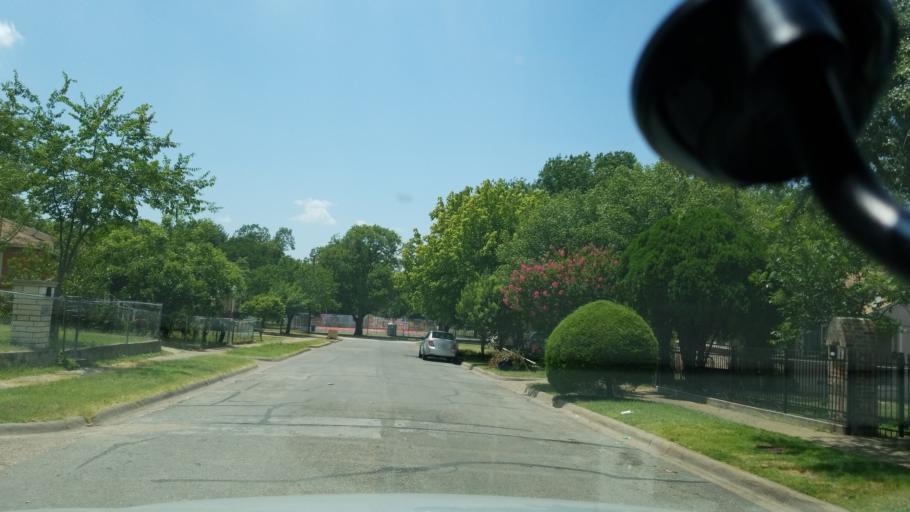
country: US
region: Texas
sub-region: Dallas County
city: Cockrell Hill
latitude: 32.7320
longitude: -96.8759
